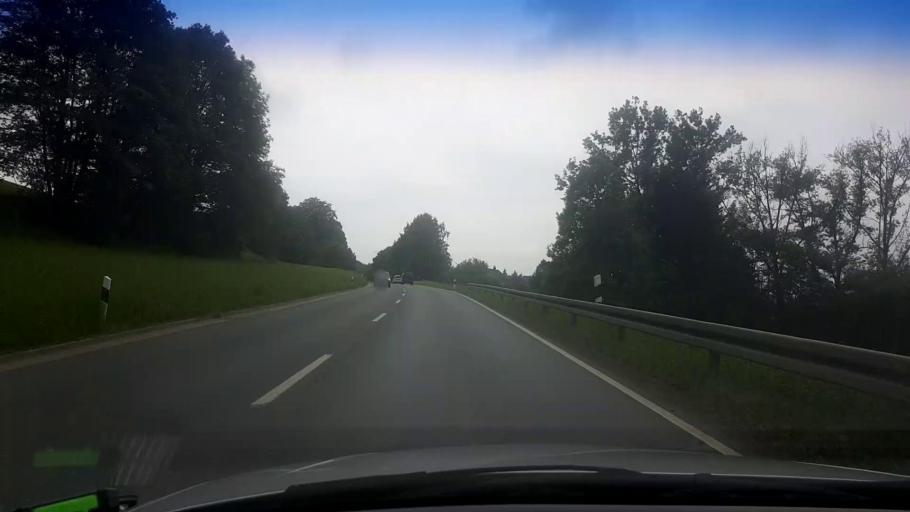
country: DE
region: Bavaria
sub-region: Upper Franconia
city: Gesees
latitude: 50.0396
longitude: 11.6591
